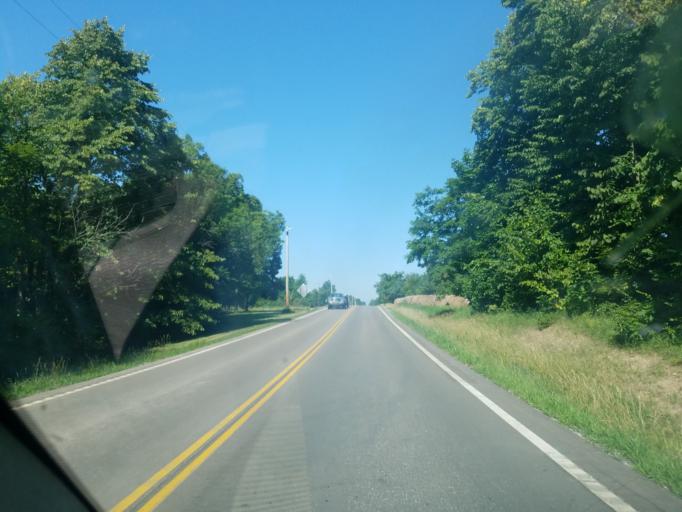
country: US
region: Ohio
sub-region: Logan County
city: Northwood
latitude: 40.4544
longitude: -83.7329
